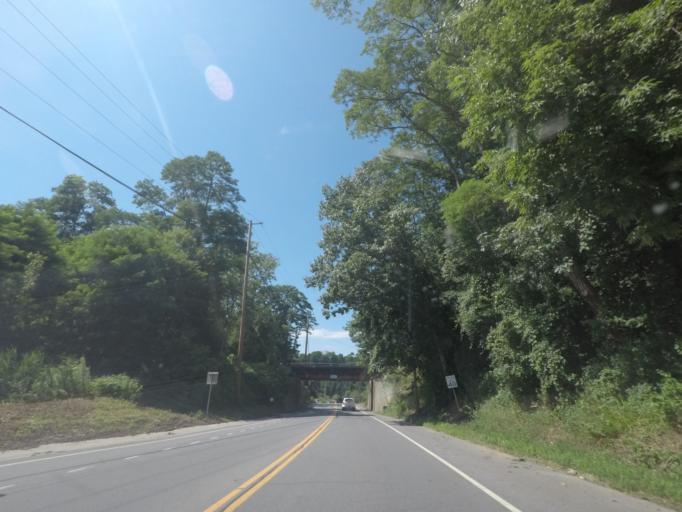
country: US
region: New York
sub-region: Schenectady County
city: Rotterdam
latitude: 42.8058
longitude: -73.9909
